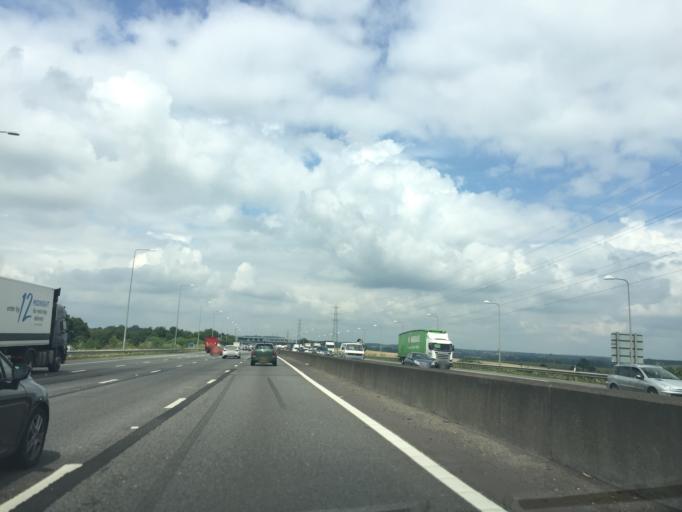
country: GB
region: England
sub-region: Buckinghamshire
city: Chalfont Saint Peter
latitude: 51.6014
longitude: -0.5301
